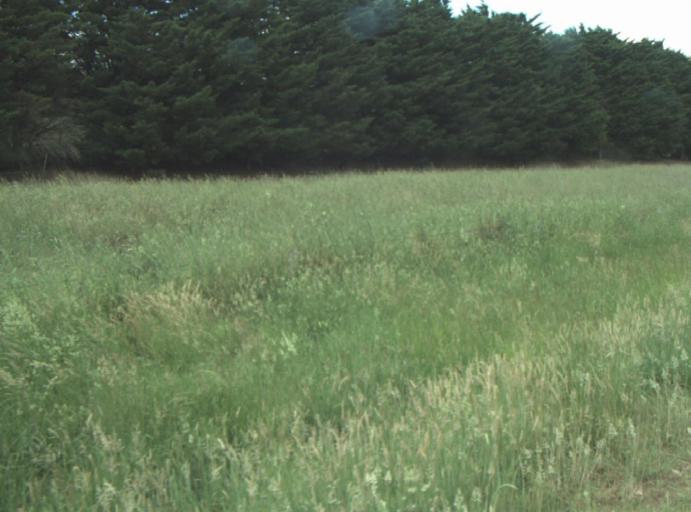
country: AU
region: Victoria
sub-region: Greater Geelong
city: Wandana Heights
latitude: -38.1948
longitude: 144.2643
